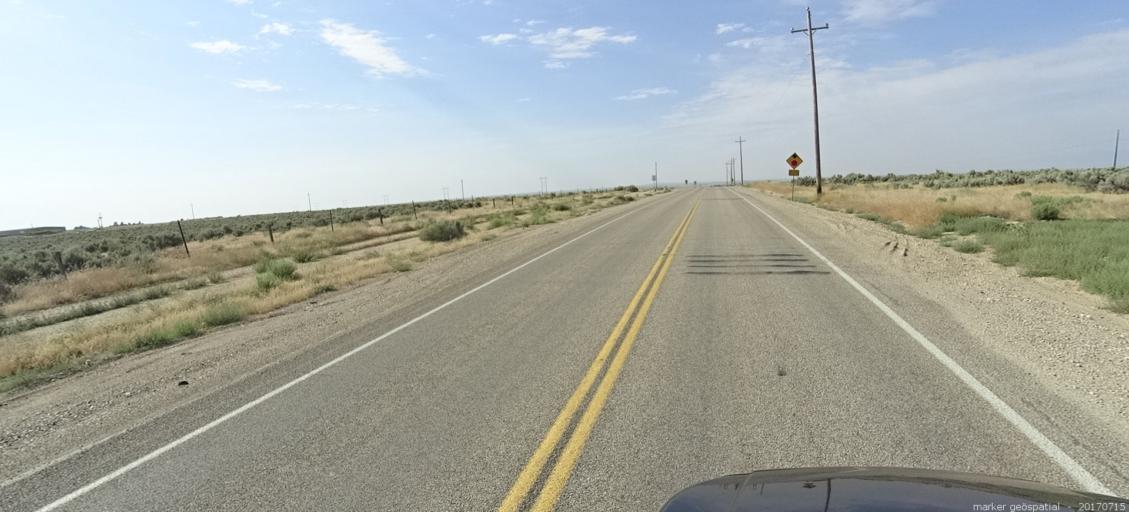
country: US
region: Idaho
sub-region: Ada County
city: Boise
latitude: 43.4612
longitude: -116.2344
